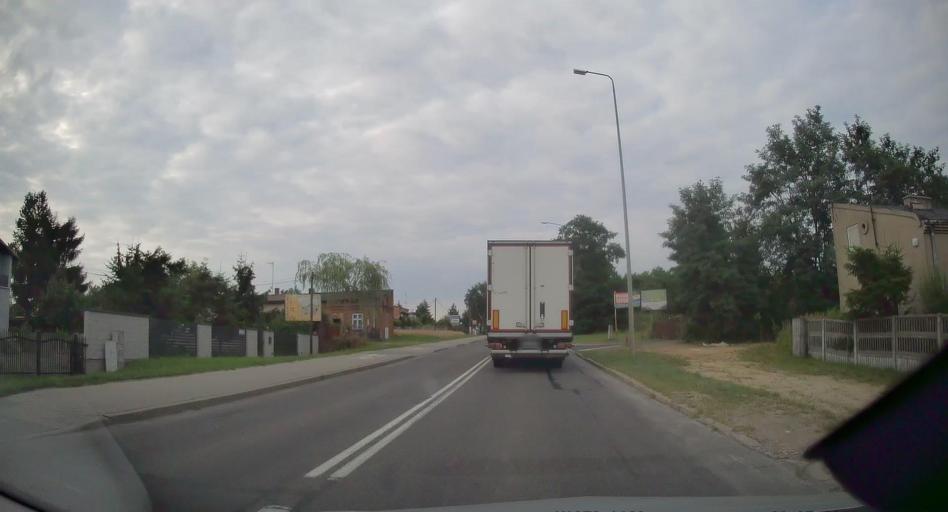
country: PL
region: Lodz Voivodeship
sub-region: Powiat radomszczanski
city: Radomsko
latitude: 51.0506
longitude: 19.4395
